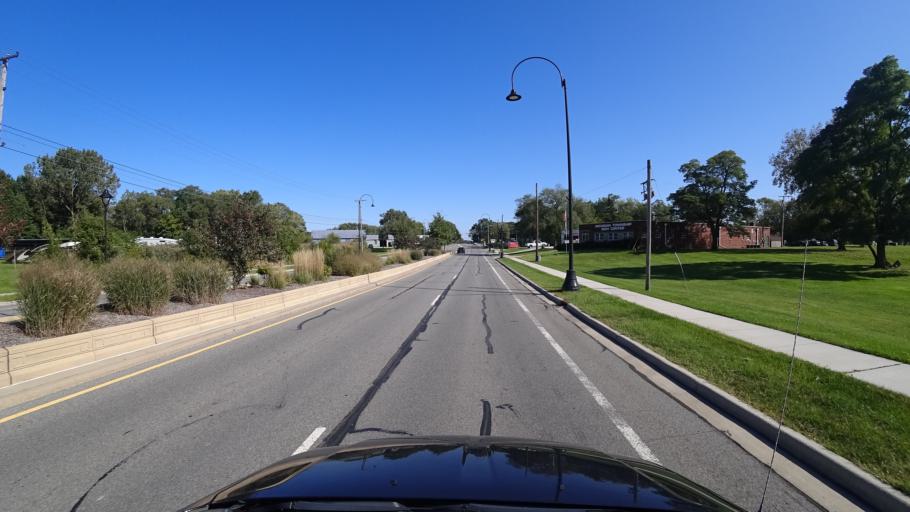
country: US
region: Indiana
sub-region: LaPorte County
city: Trail Creek
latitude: 41.7081
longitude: -86.8673
